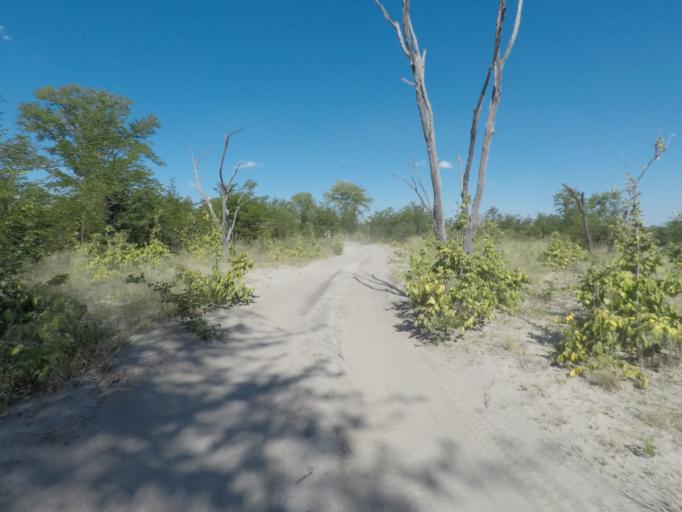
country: BW
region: North West
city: Maun
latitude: -19.4239
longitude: 23.6381
